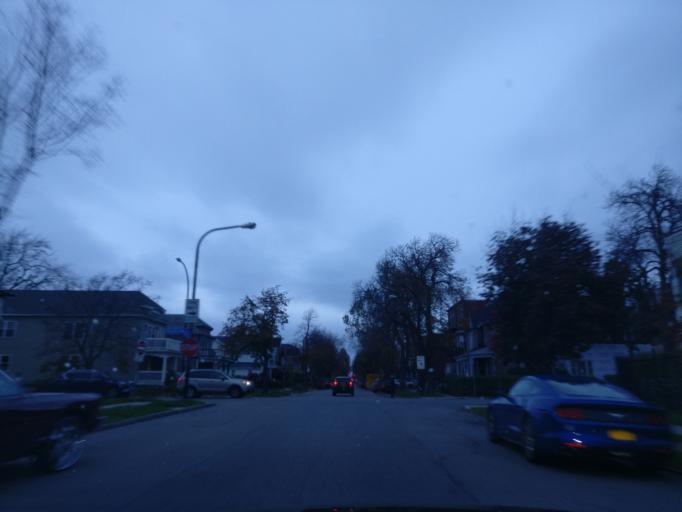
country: US
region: New York
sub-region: Erie County
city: Buffalo
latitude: 42.8969
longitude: -78.8863
